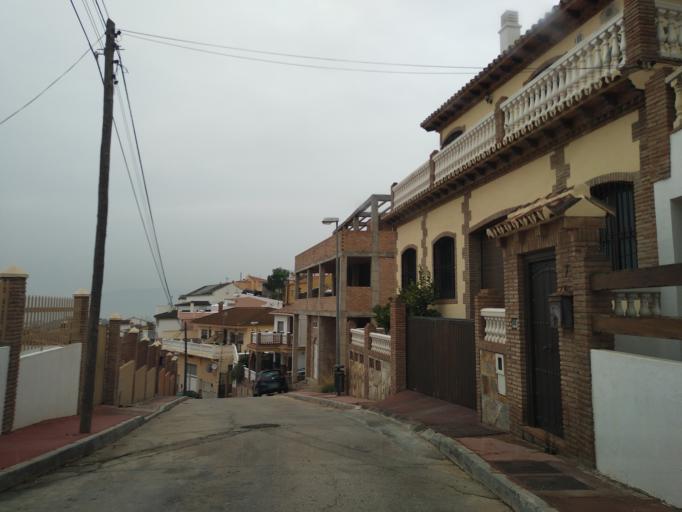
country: ES
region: Andalusia
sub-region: Provincia de Malaga
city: Malaga
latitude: 36.7475
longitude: -4.4776
